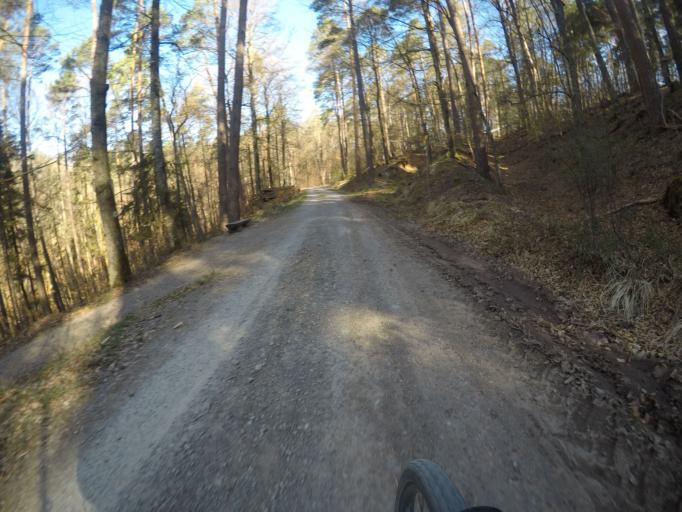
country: DE
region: Baden-Wuerttemberg
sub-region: Regierungsbezirk Stuttgart
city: Waldenbuch
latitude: 48.6067
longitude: 9.1501
